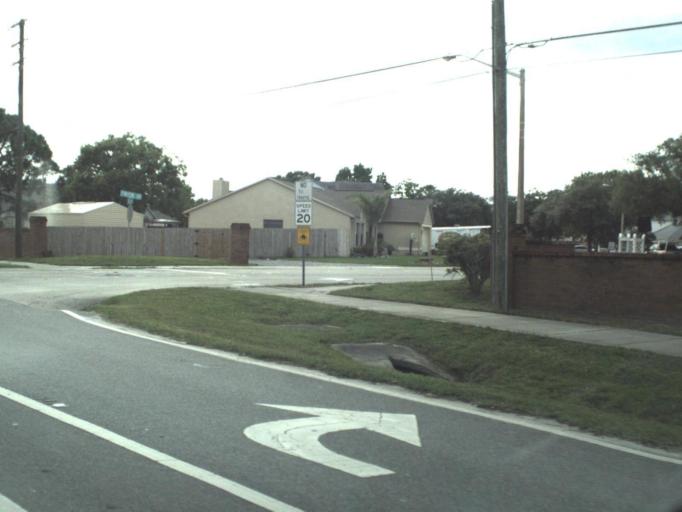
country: US
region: Florida
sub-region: Brevard County
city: Cocoa West
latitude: 28.3886
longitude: -80.7830
